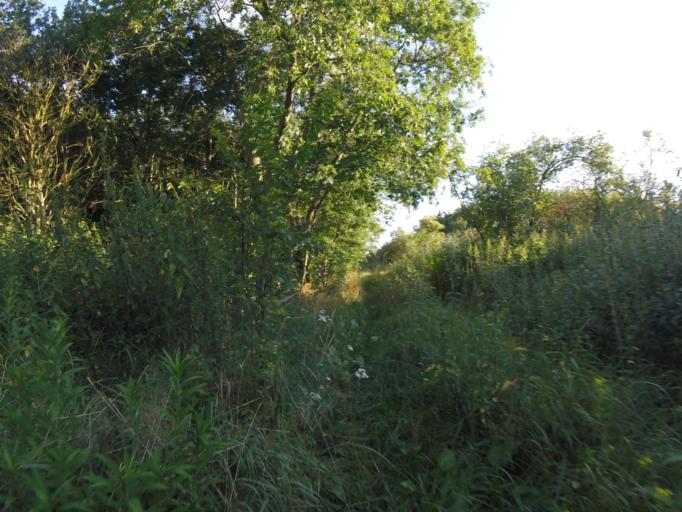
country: DE
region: Brandenburg
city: Schulzendorf
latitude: 52.3168
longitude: 13.5593
